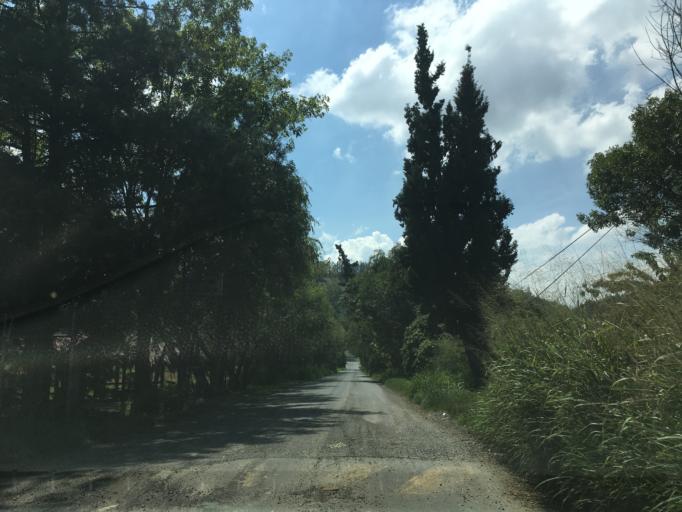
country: MX
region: Michoacan
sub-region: Morelia
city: La Mintzita (Piedra Dura)
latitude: 19.6436
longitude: -101.2663
